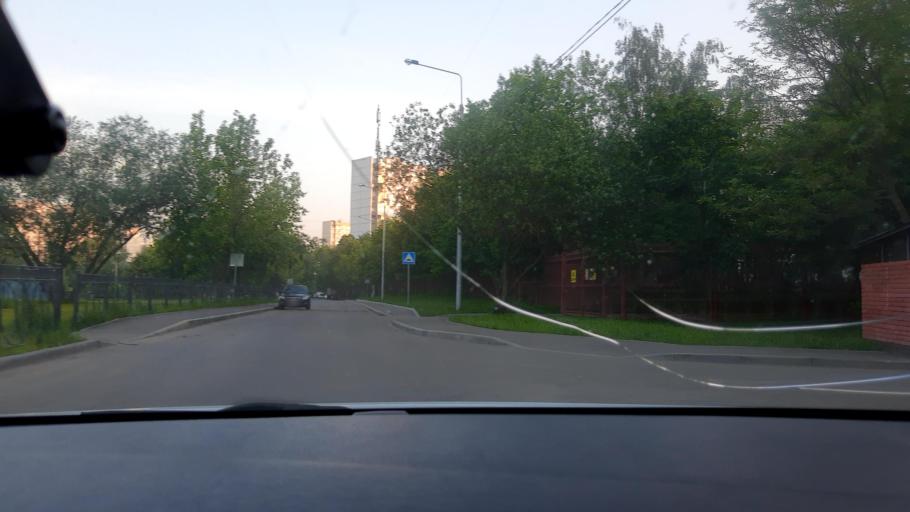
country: RU
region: Moscow
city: Solntsevo
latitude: 55.6469
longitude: 37.4043
